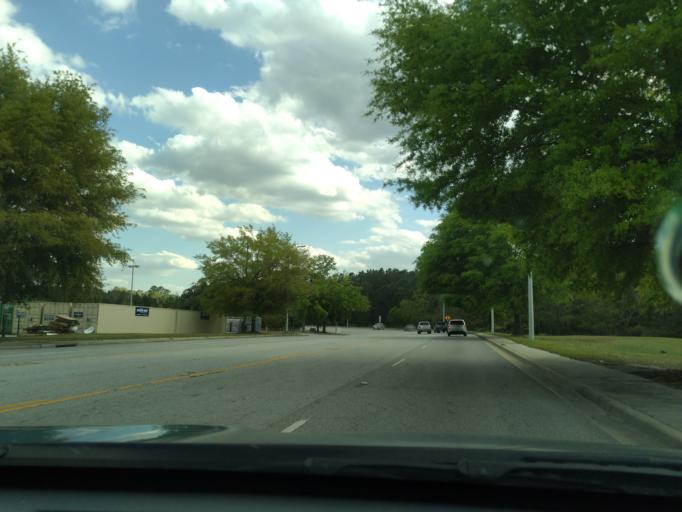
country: US
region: South Carolina
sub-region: Florence County
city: Florence
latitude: 34.1593
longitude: -79.7598
